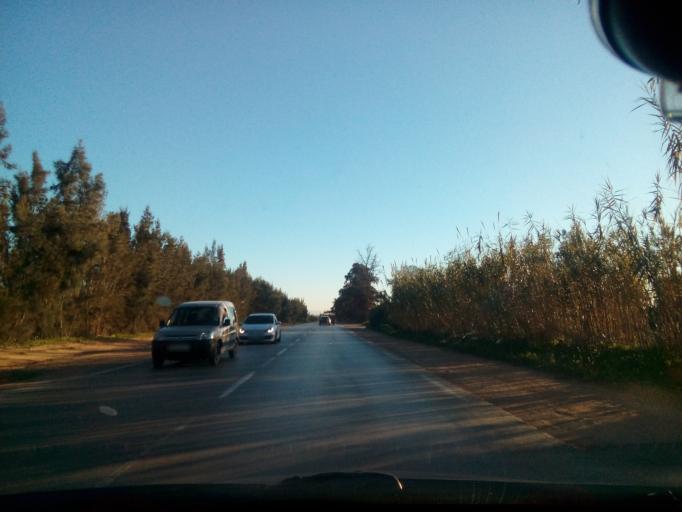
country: DZ
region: Mostaganem
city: Mostaganem
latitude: 35.8107
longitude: 0.1709
